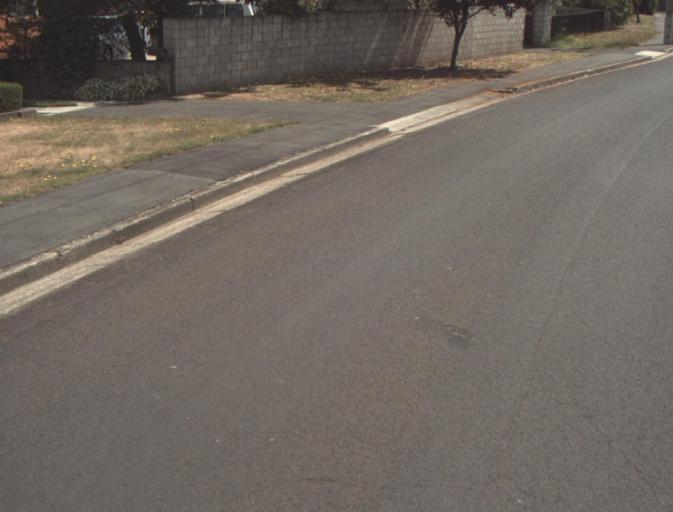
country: AU
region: Tasmania
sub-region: Launceston
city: Newnham
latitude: -41.4111
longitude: 147.1524
